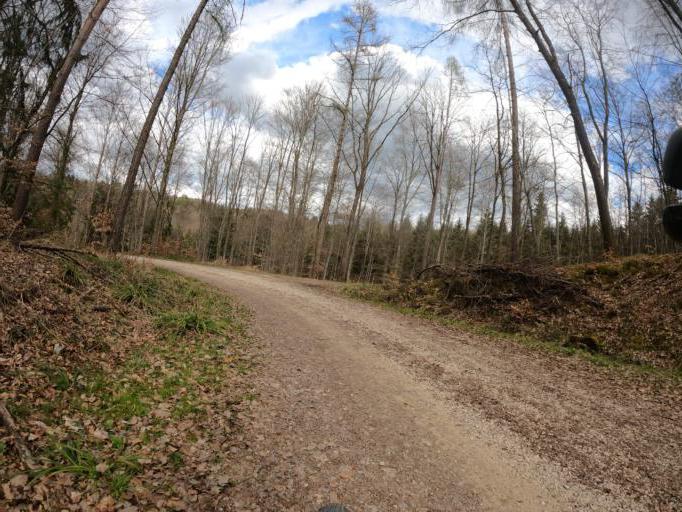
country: DE
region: Baden-Wuerttemberg
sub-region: Tuebingen Region
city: Gomaringen
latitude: 48.4319
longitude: 9.1198
